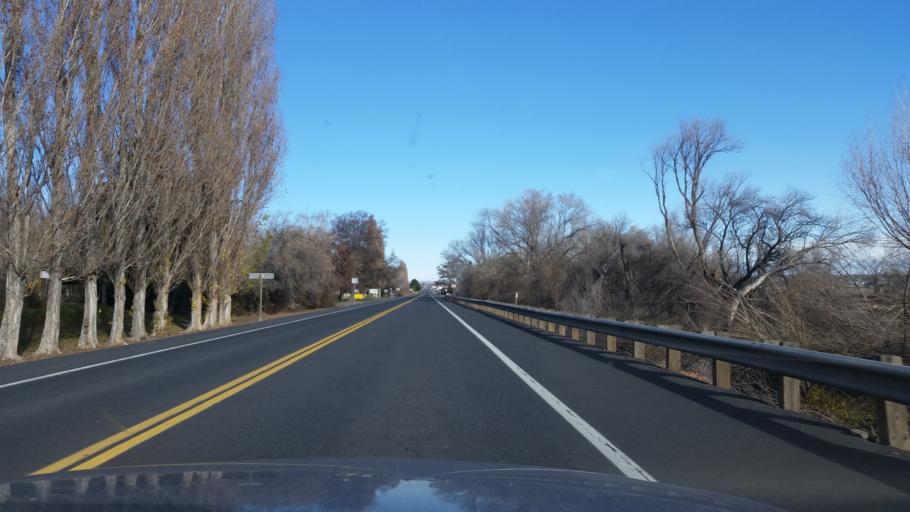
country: US
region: Washington
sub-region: Grant County
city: Ephrata
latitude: 47.2827
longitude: -119.5790
